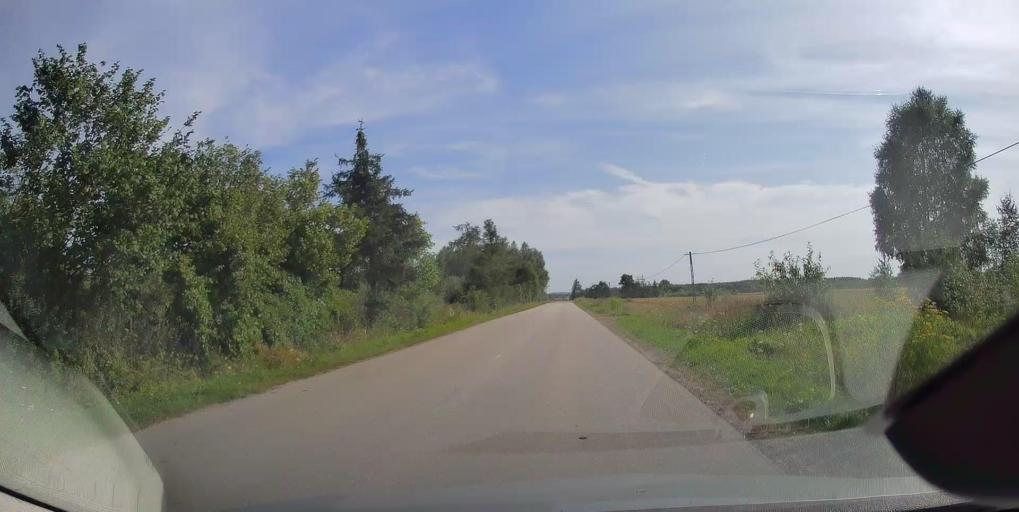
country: PL
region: Lodz Voivodeship
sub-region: Powiat opoczynski
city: Mniszkow
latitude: 51.3696
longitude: 20.0395
